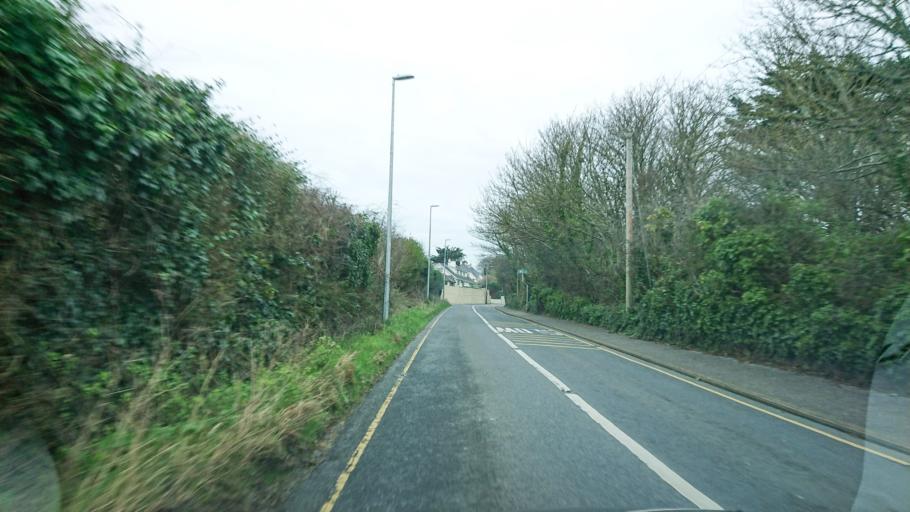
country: IE
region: Munster
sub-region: Waterford
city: Tra Mhor
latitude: 52.1539
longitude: -7.1608
